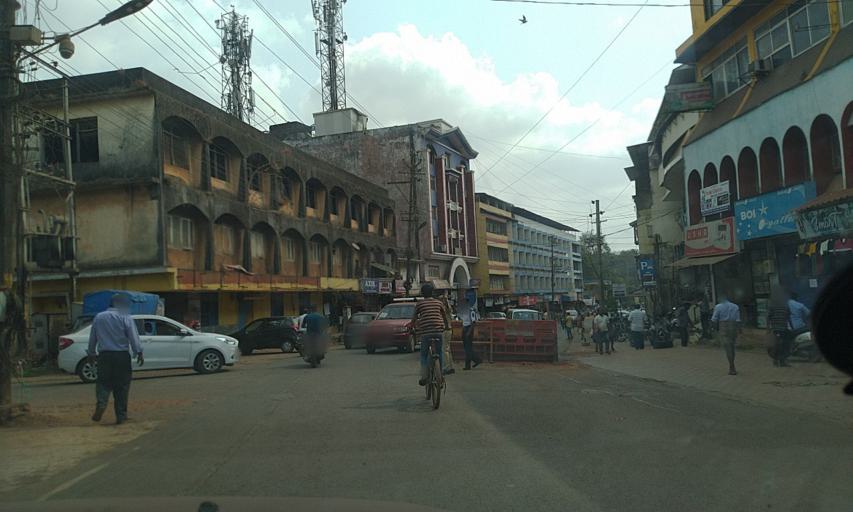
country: IN
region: Goa
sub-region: North Goa
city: Ponda
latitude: 15.4014
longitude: 74.0059
